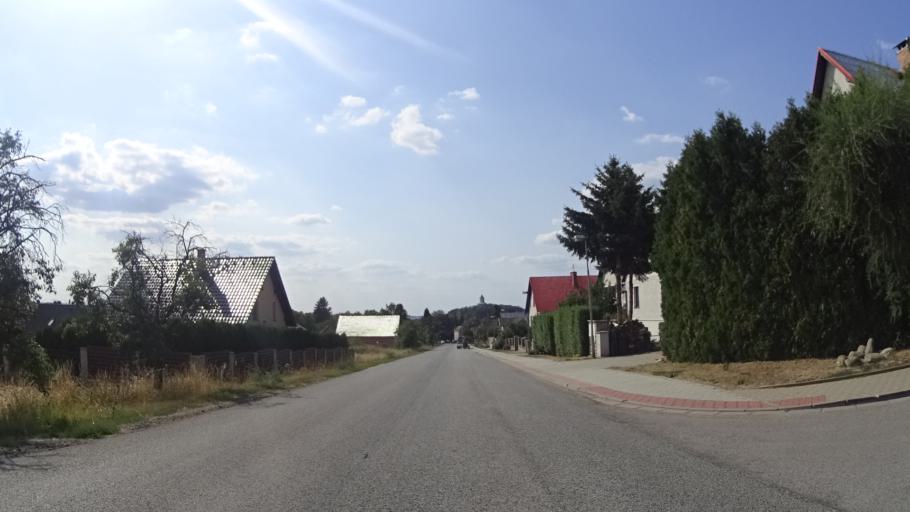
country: CZ
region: Kralovehradecky
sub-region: Okres Jicin
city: Sobotka
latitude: 50.4672
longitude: 15.1871
